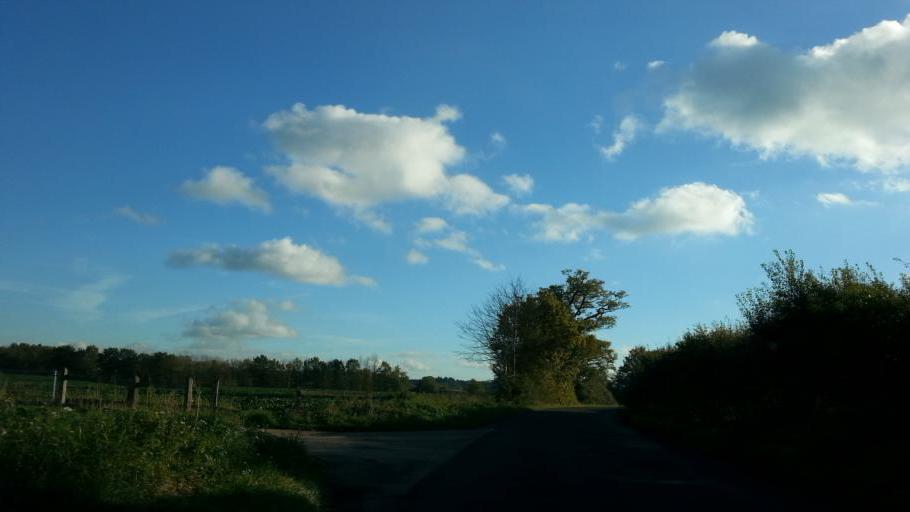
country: GB
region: England
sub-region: Suffolk
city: Thurston
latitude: 52.2387
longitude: 0.8077
